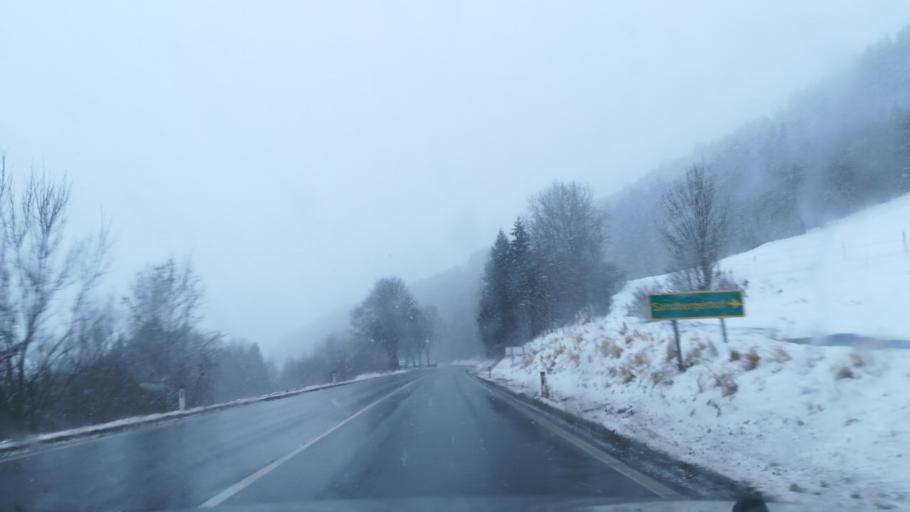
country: AT
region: Styria
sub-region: Politischer Bezirk Murtal
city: Poels
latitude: 47.2025
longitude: 14.5871
